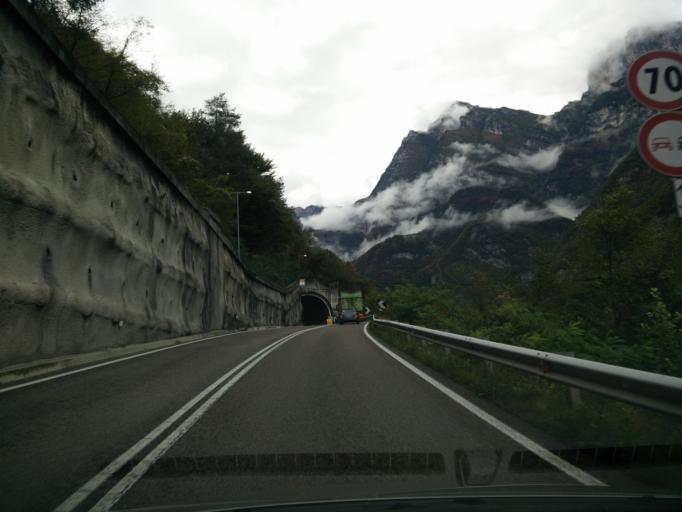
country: IT
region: Veneto
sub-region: Provincia di Belluno
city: Castello Lavazzo
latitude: 46.2966
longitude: 12.3124
